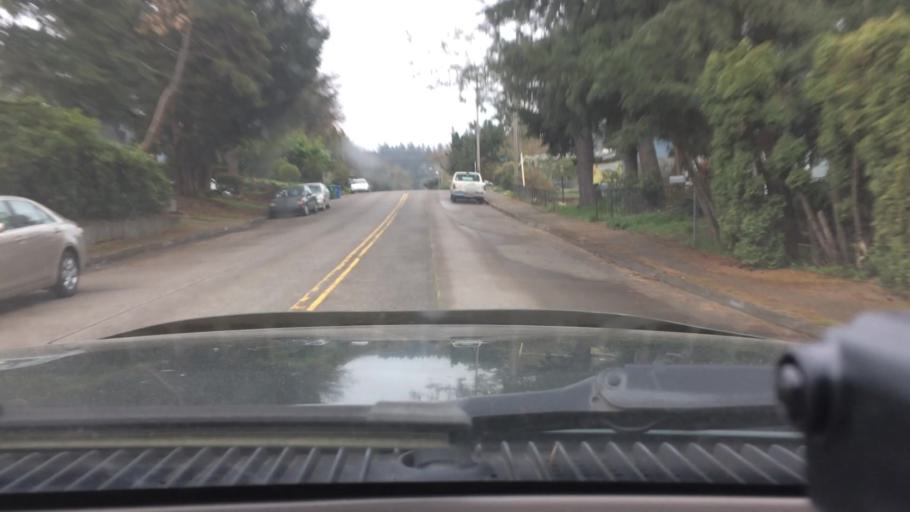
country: US
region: Oregon
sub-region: Lane County
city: Eugene
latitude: 44.0328
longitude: -123.1013
